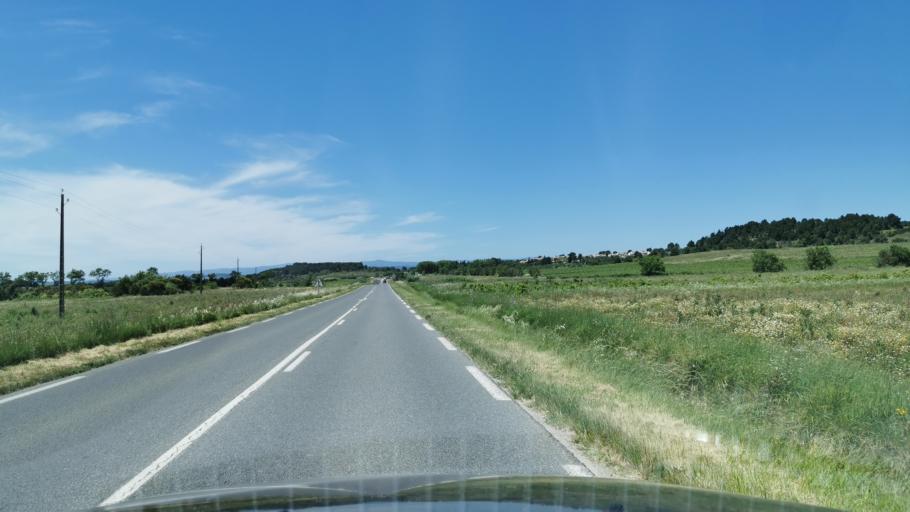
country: FR
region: Languedoc-Roussillon
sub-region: Departement de l'Aude
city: Marcorignan
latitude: 43.2135
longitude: 2.9352
